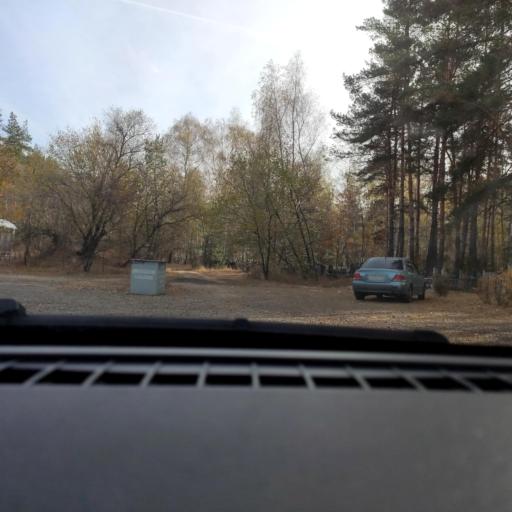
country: RU
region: Voronezj
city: Maslovka
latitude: 51.5775
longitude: 39.2954
